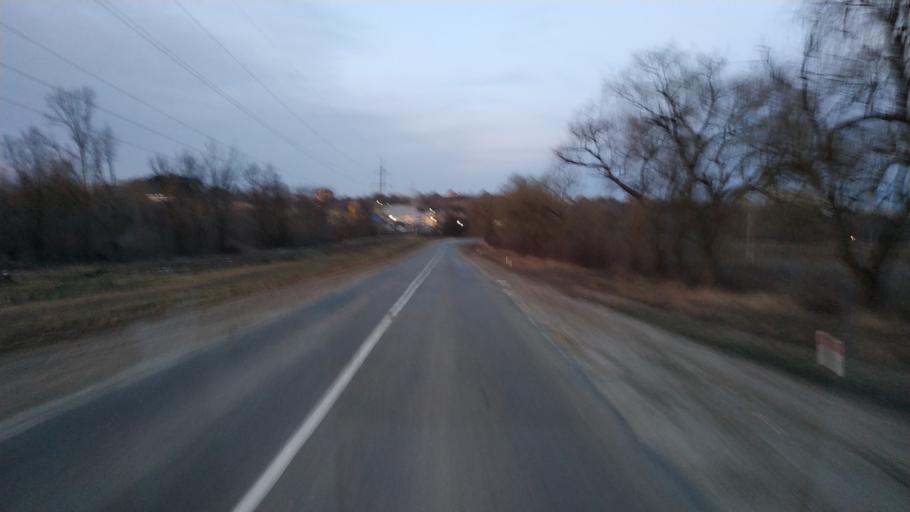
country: MD
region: Laloveni
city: Ialoveni
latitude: 46.9546
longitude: 28.7472
